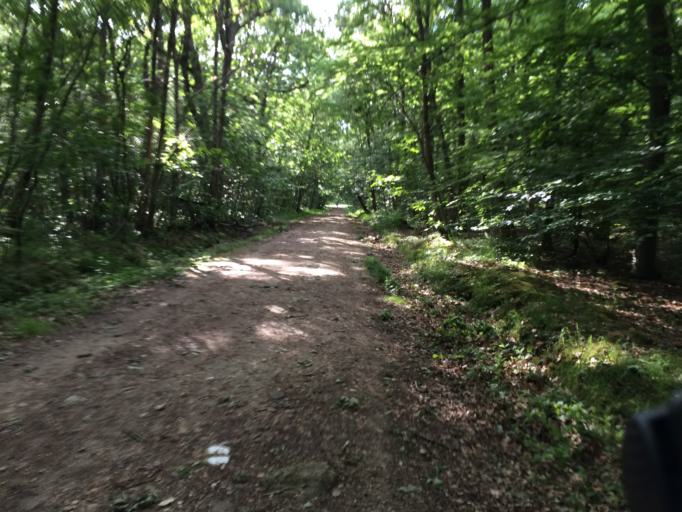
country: FR
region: Ile-de-France
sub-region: Departement de l'Essonne
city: Igny
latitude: 48.7511
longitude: 2.2437
